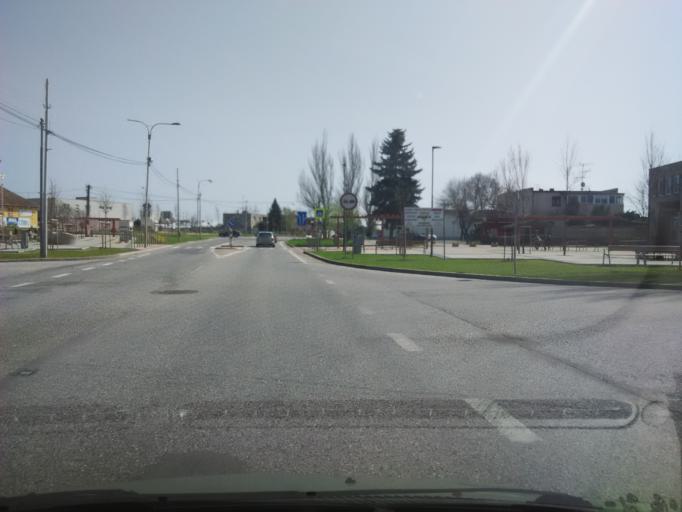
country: SK
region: Nitriansky
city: Surany
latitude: 48.0951
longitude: 18.0639
